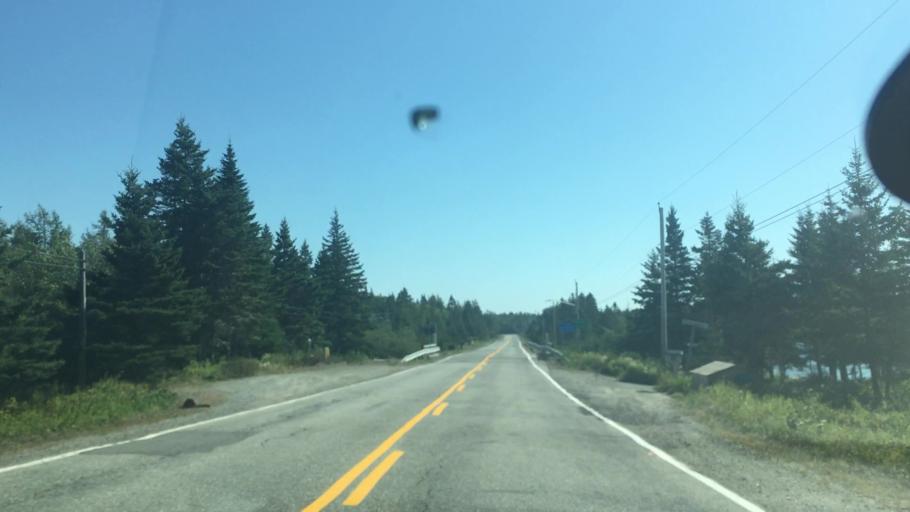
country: CA
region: Nova Scotia
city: New Glasgow
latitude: 44.9036
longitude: -62.4106
